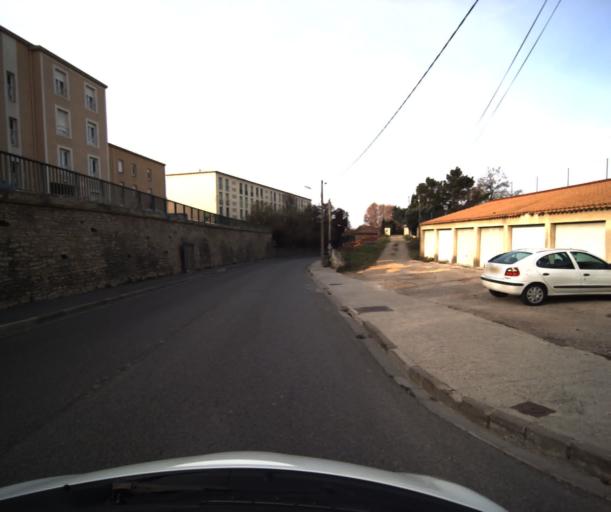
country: FR
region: Provence-Alpes-Cote d'Azur
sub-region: Departement du Vaucluse
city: Pertuis
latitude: 43.6914
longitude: 5.4957
